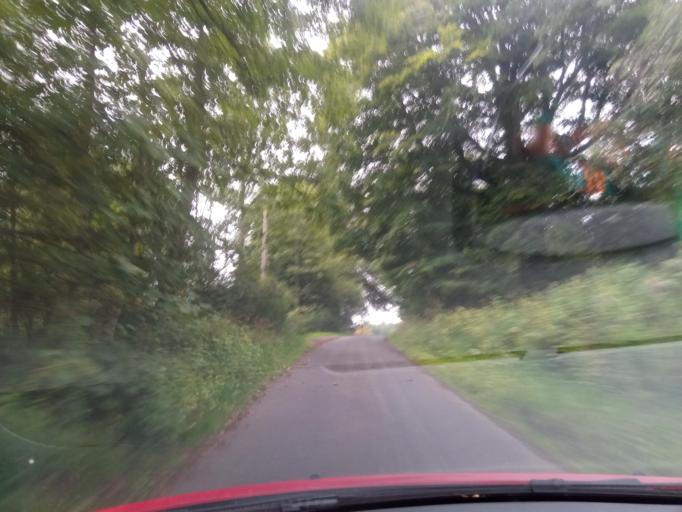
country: GB
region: Scotland
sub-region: Fife
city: Pathhead
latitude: 55.7415
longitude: -2.9214
